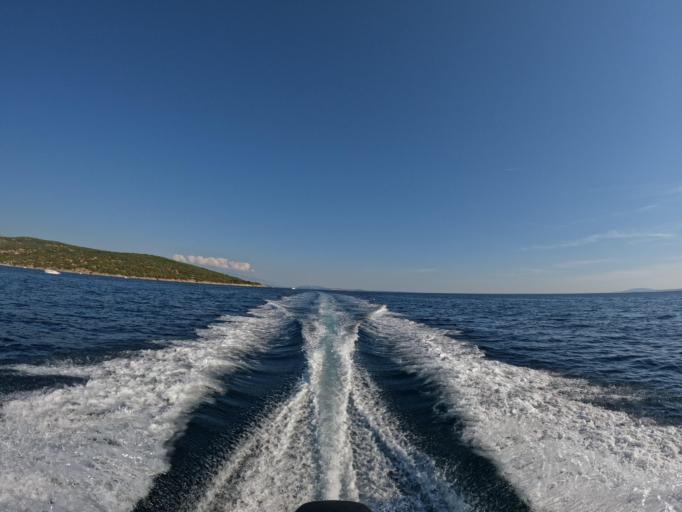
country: HR
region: Primorsko-Goranska
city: Punat
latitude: 44.9876
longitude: 14.6079
